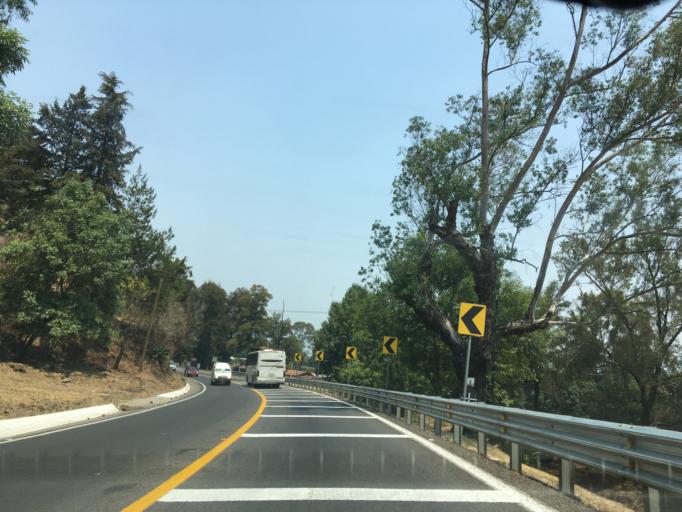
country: MX
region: Michoacan
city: Patzcuaro
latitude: 19.5470
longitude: -101.5931
